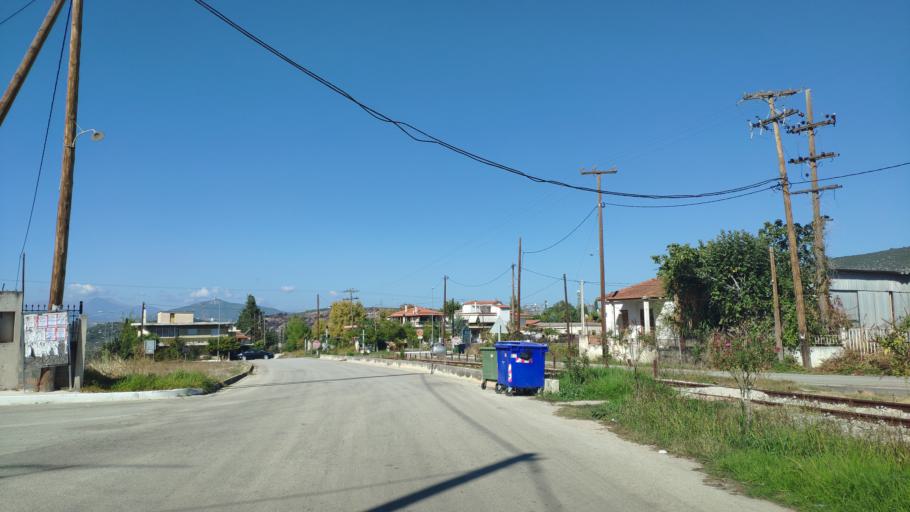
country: GR
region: Peloponnese
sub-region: Nomos Korinthias
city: Khiliomodhi
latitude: 37.8076
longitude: 22.8668
